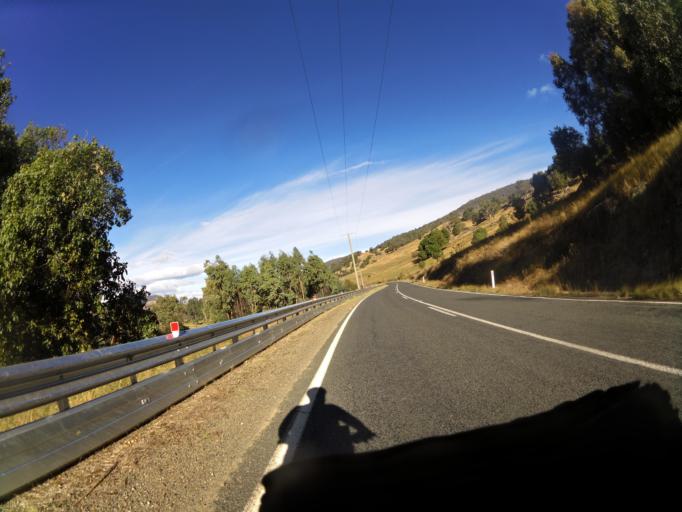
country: AU
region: New South Wales
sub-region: Greater Hume Shire
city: Holbrook
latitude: -35.9655
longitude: 147.7662
